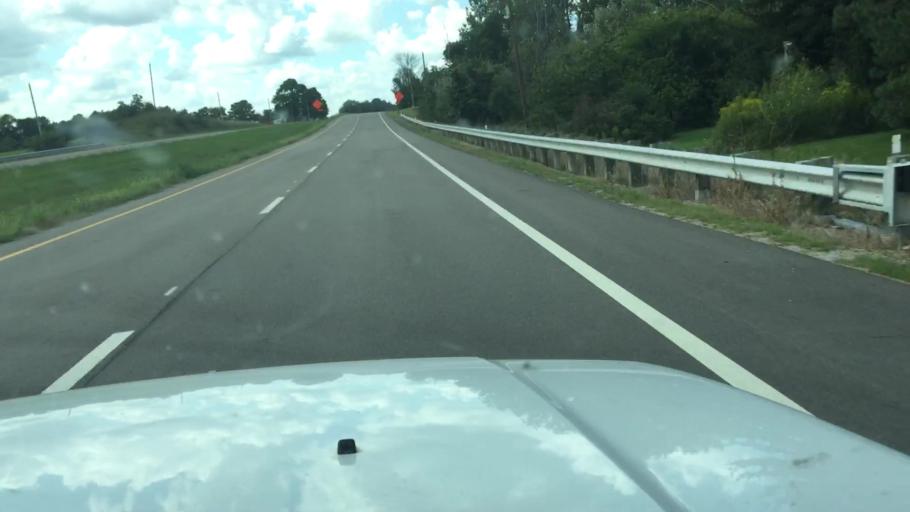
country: US
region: Ohio
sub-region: Madison County
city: Choctaw Lake
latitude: 39.9309
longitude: -83.5450
